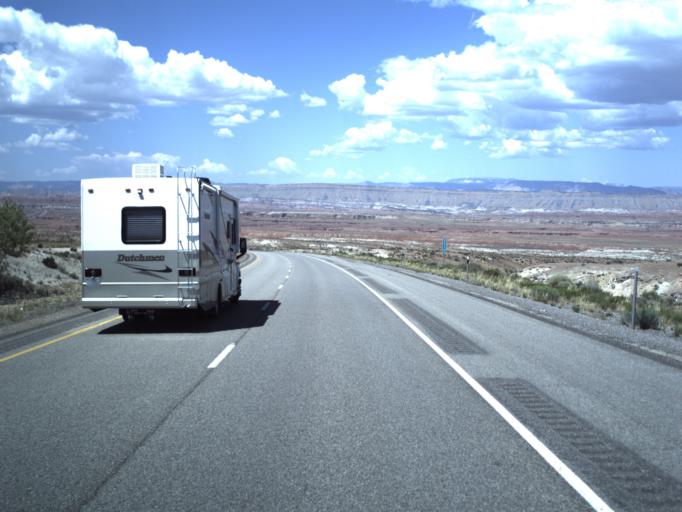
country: US
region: Utah
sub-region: Emery County
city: Ferron
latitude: 38.8462
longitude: -110.9908
